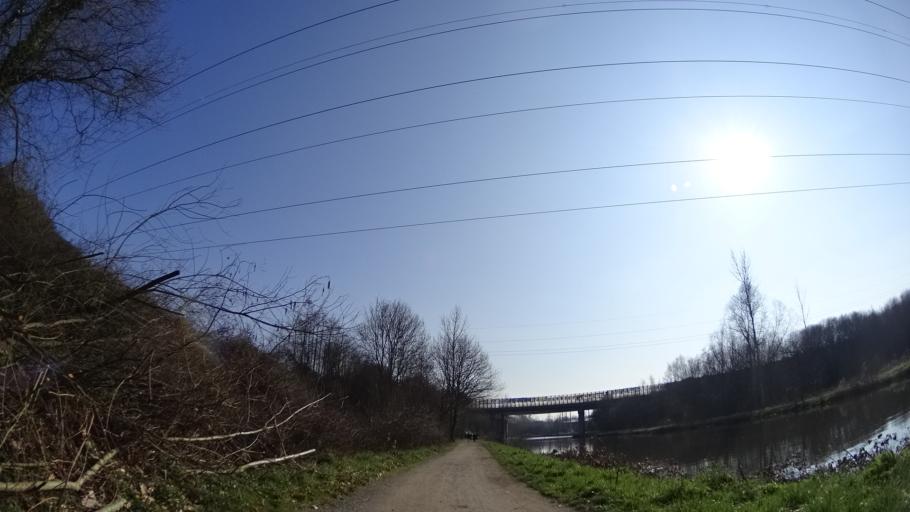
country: FR
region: Brittany
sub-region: Departement d'Ille-et-Vilaine
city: Saint-Gregoire
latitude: 48.1428
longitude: -1.6749
